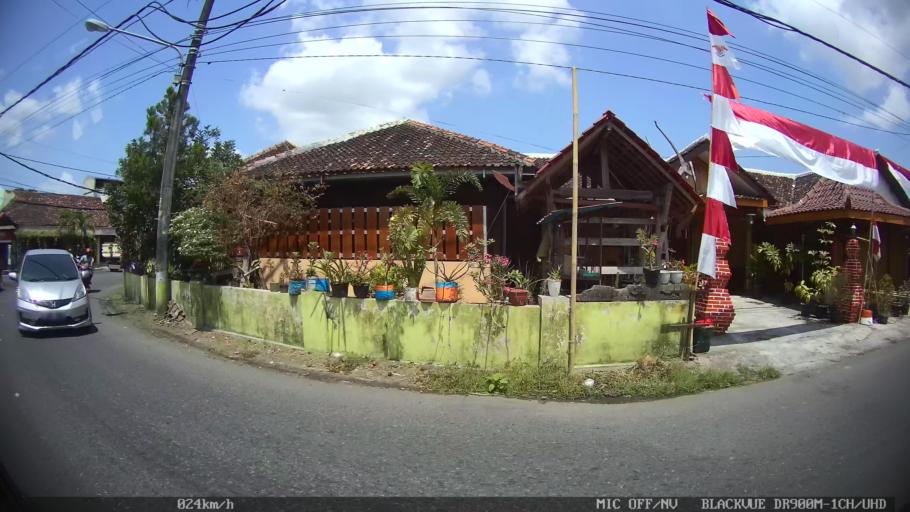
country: ID
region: Daerah Istimewa Yogyakarta
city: Sewon
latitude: -7.8947
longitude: 110.3499
